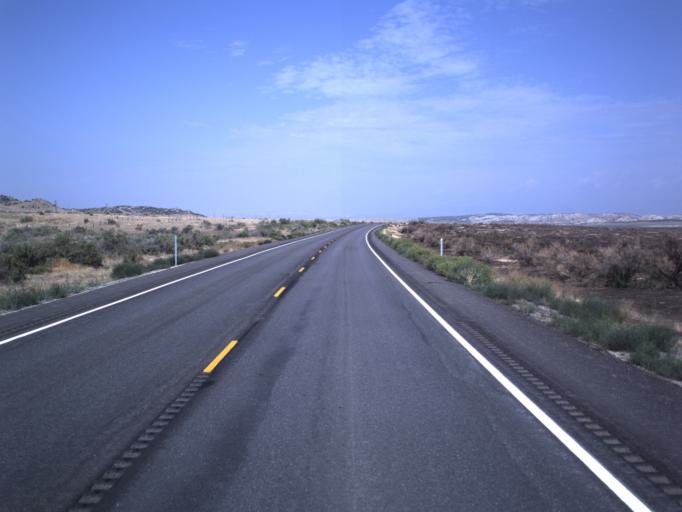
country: US
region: Utah
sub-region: Uintah County
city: Naples
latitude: 40.2927
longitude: -109.1729
